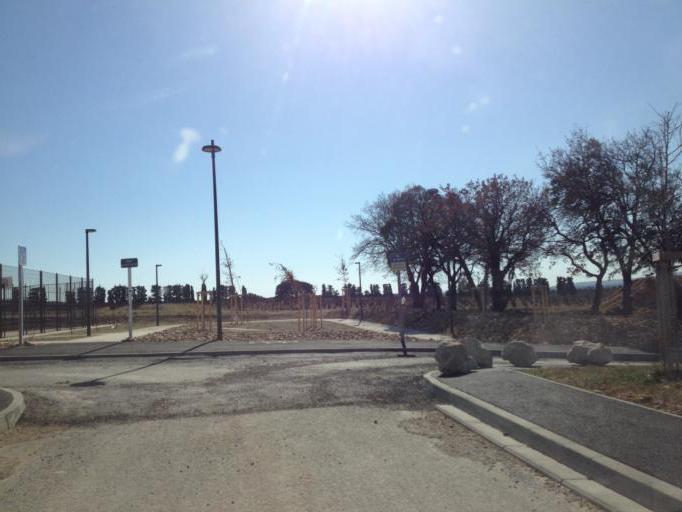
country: FR
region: Provence-Alpes-Cote d'Azur
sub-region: Departement du Vaucluse
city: Bedarrides
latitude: 44.0328
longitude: 4.8951
